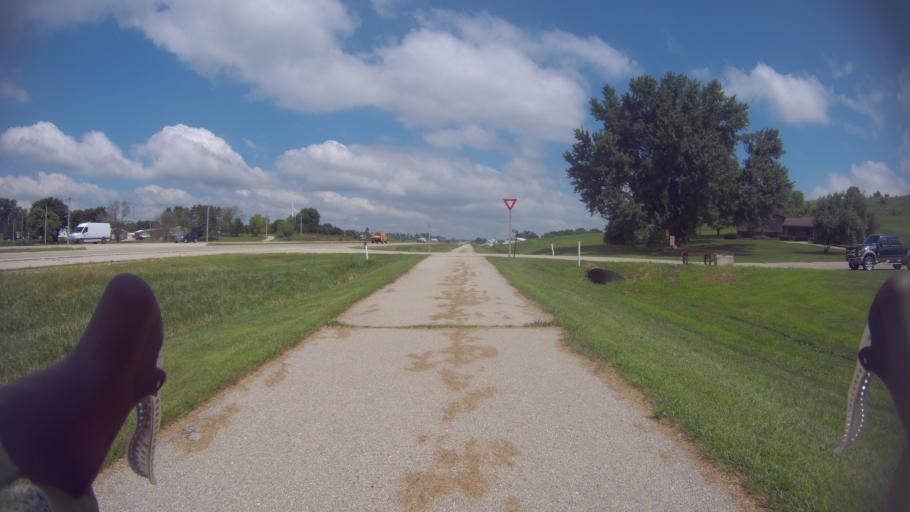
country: US
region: Wisconsin
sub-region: Dane County
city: Middleton
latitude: 43.1662
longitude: -89.5357
